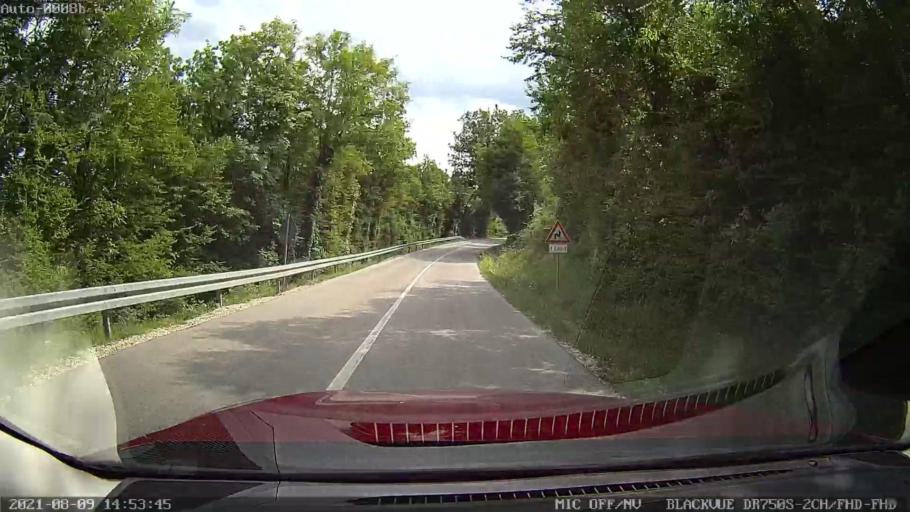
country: HR
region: Istarska
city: Pazin
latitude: 45.2825
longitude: 14.0760
